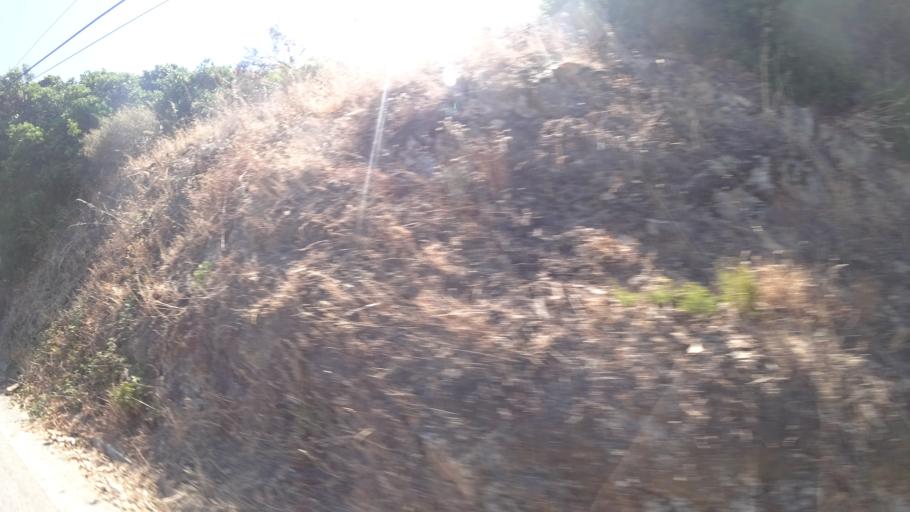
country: FR
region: Corsica
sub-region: Departement de la Corse-du-Sud
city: Alata
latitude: 41.9809
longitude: 8.6767
